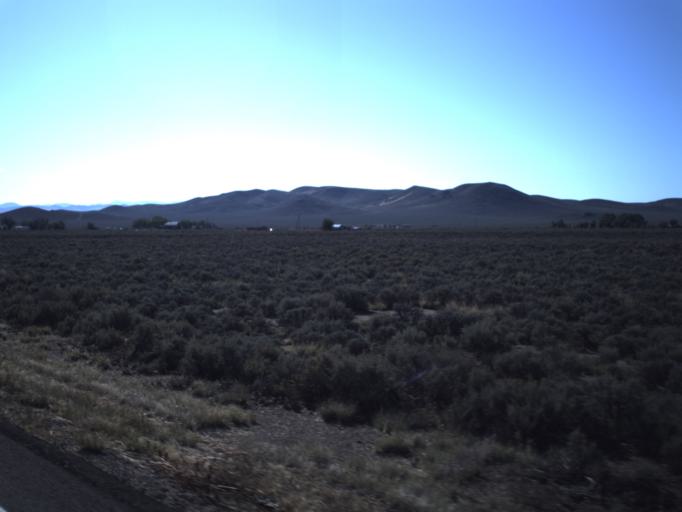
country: US
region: Utah
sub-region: Washington County
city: Enterprise
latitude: 37.7512
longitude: -113.7733
